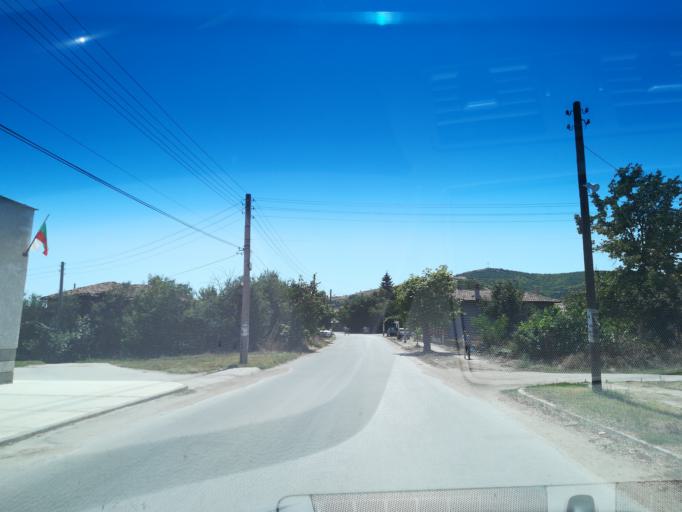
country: BG
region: Pazardzhik
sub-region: Obshtina Pazardzhik
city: Pazardzhik
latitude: 42.3353
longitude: 24.4007
